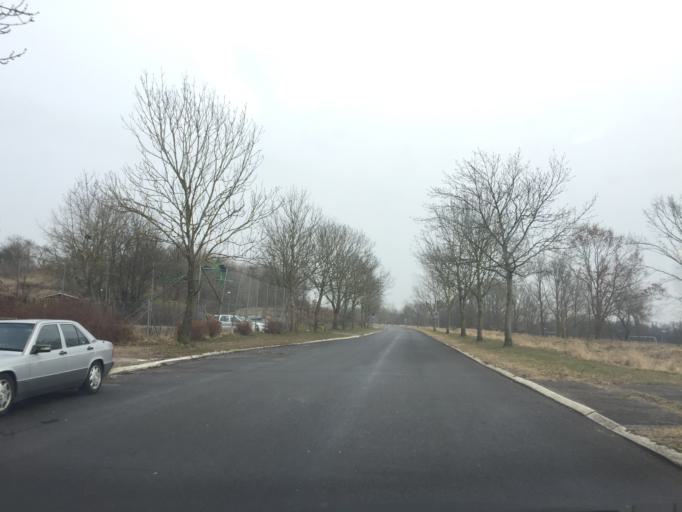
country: DK
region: Capital Region
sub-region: Hoje-Taastrup Kommune
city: Flong
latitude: 55.6477
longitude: 12.2112
